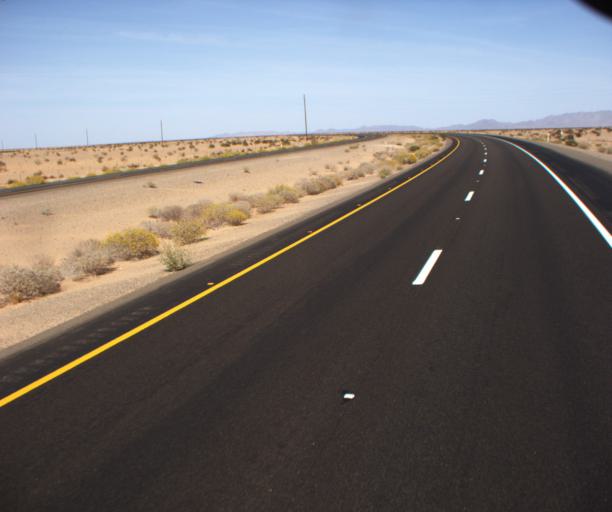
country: US
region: Arizona
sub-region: Yuma County
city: Somerton
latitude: 32.4966
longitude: -114.5640
